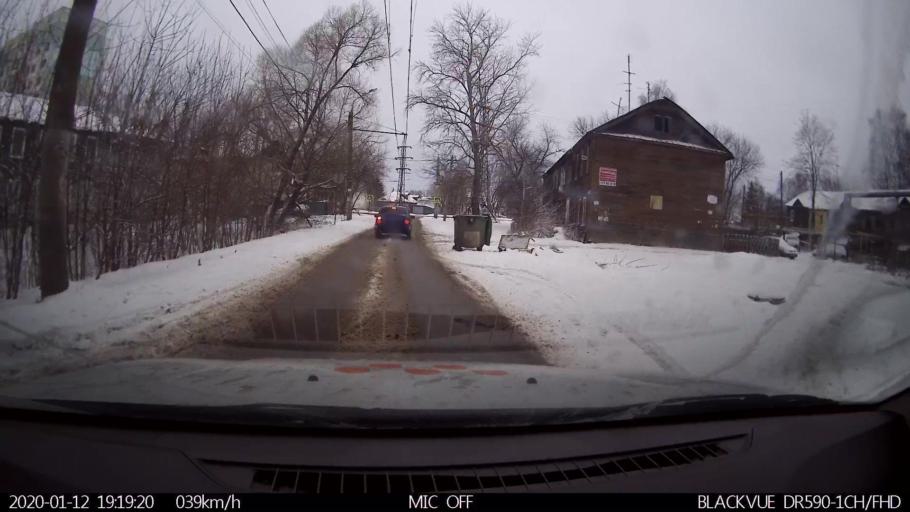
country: RU
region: Nizjnij Novgorod
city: Nizhniy Novgorod
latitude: 56.2897
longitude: 43.9083
